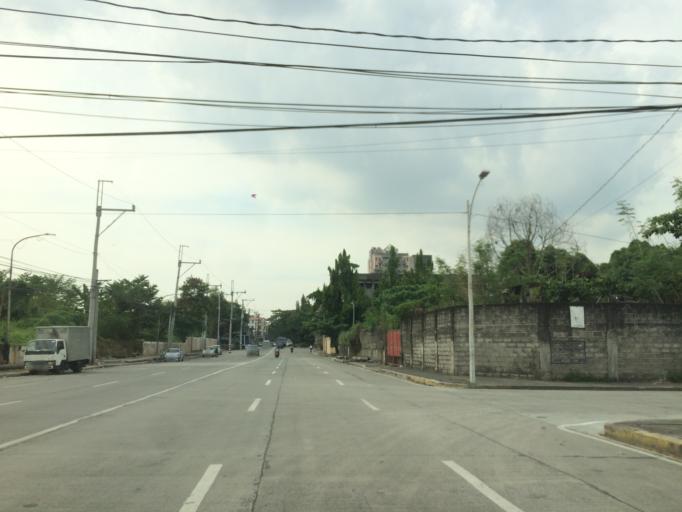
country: PH
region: Calabarzon
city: Del Monte
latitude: 14.6319
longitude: 121.0074
